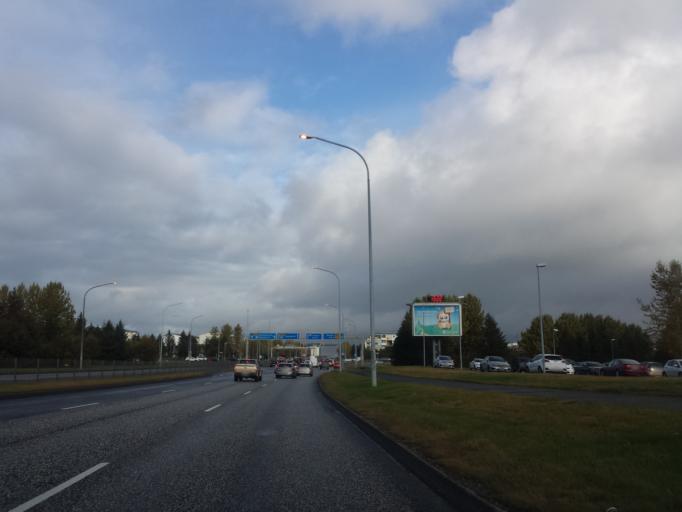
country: IS
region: Capital Region
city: Reykjavik
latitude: 64.1311
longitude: -21.8994
